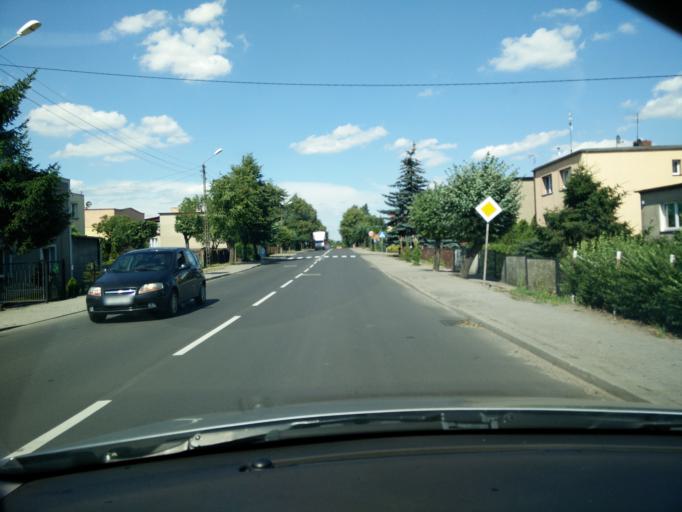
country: PL
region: Greater Poland Voivodeship
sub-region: Powiat sredzki
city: Sroda Wielkopolska
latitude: 52.2277
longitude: 17.2901
